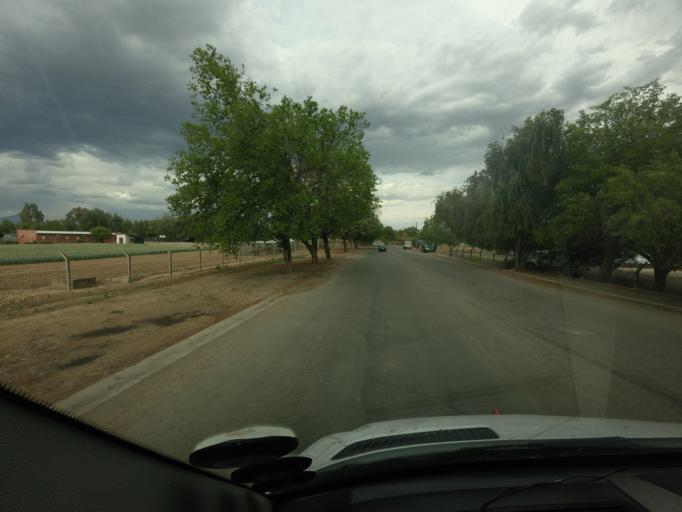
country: ZA
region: Western Cape
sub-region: Eden District Municipality
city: Oudtshoorn
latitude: -33.5832
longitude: 22.1972
